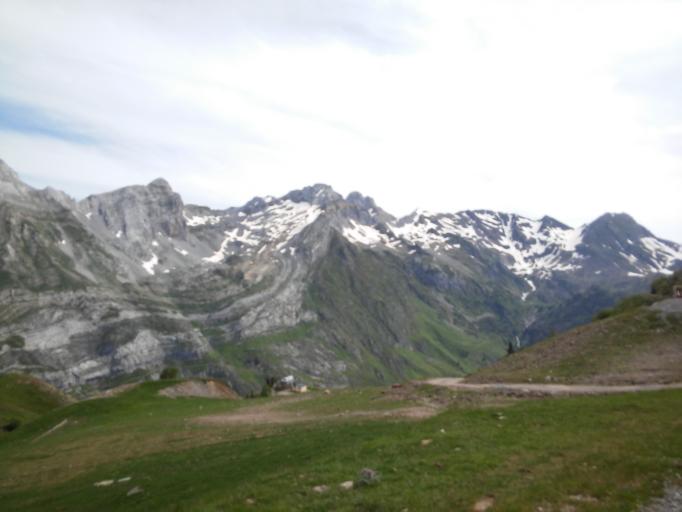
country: FR
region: Aquitaine
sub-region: Departement des Pyrenees-Atlantiques
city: Laruns
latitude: 42.8994
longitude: -0.3913
